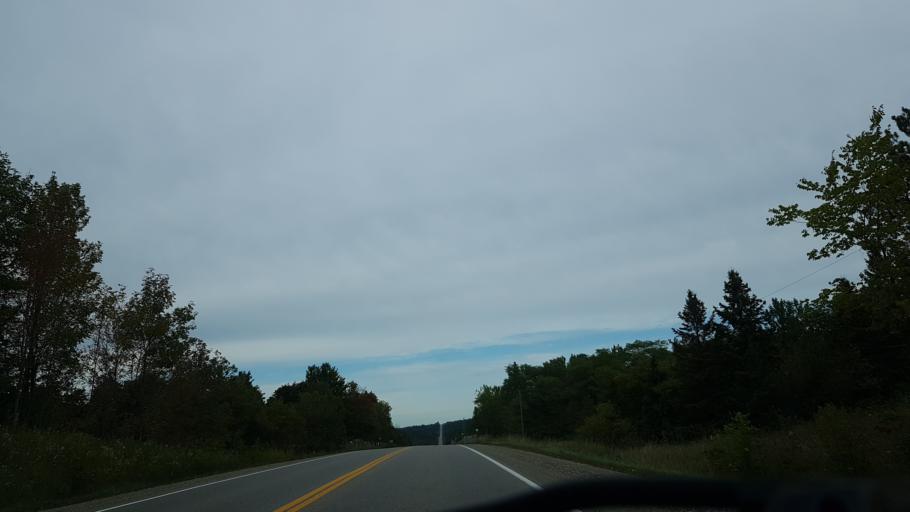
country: CA
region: Ontario
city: Orangeville
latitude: 44.0584
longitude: -80.0134
